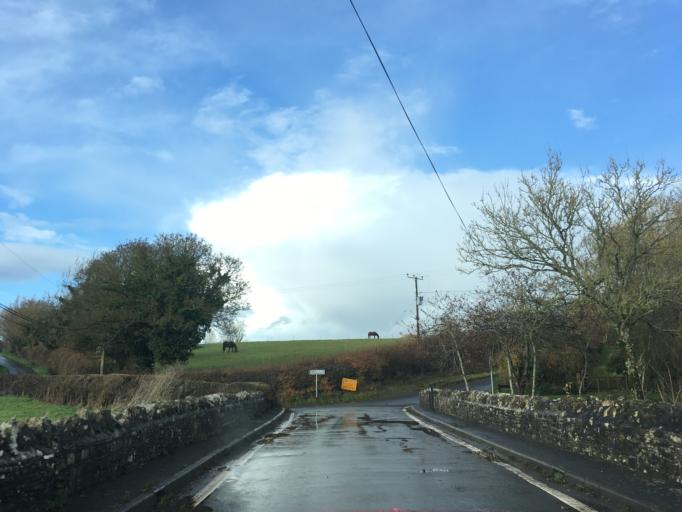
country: GB
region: England
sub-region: South Gloucestershire
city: Hinton
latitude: 51.4665
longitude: -2.4075
